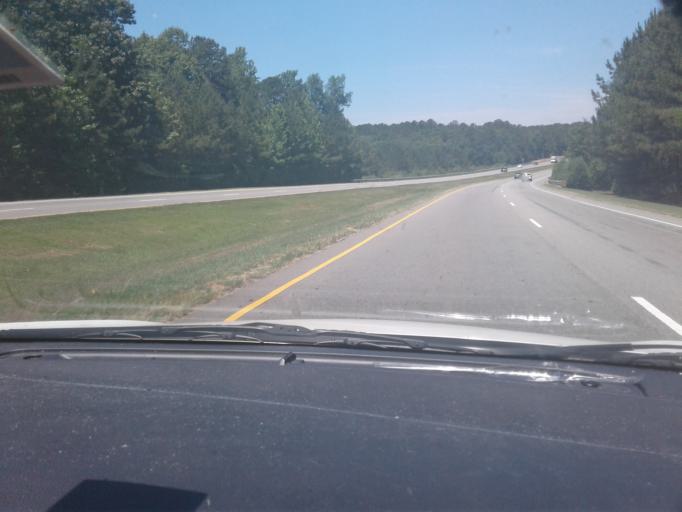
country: US
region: North Carolina
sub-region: Wake County
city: Holly Springs
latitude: 35.6458
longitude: -78.8429
